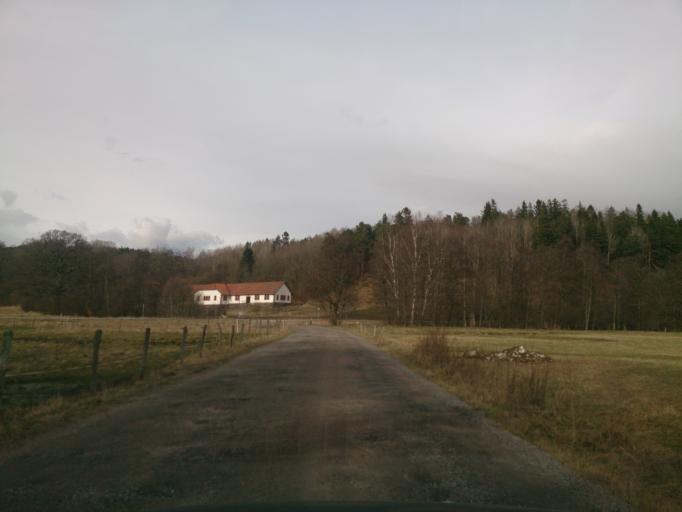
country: SE
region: OEstergoetland
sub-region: Norrkopings Kommun
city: Jursla
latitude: 58.6724
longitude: 16.1372
